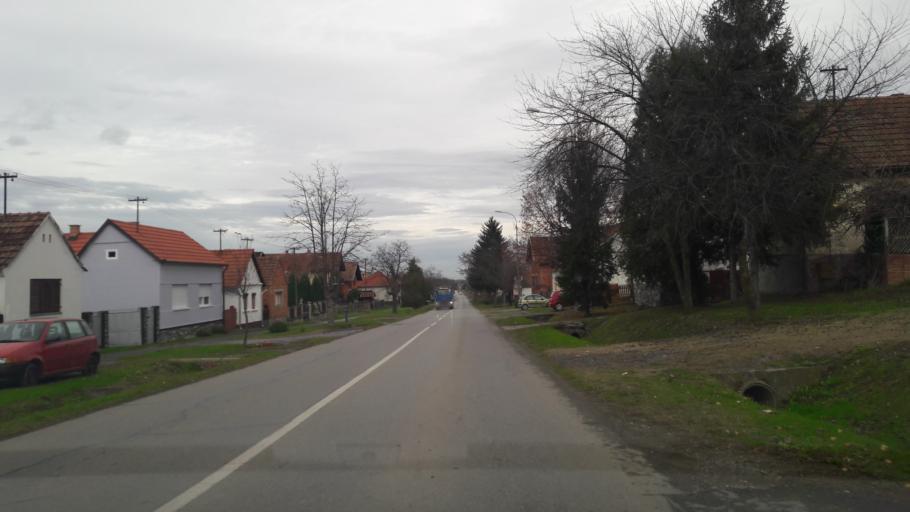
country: HR
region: Virovitick-Podravska
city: Orahovica
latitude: 45.5372
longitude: 17.8925
